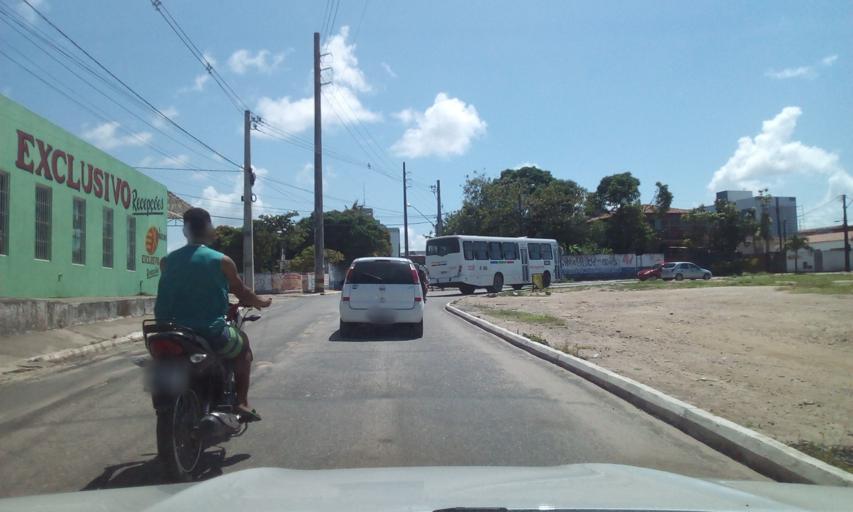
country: BR
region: Paraiba
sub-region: Conde
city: Conde
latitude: -7.2071
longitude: -34.8535
